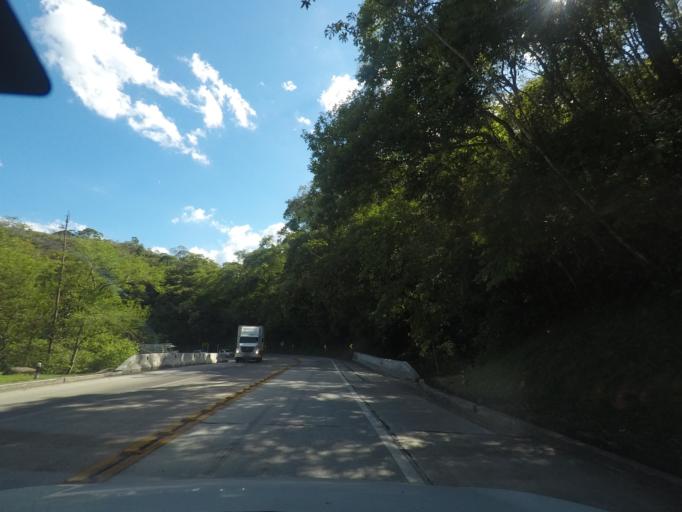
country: BR
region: Rio de Janeiro
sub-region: Guapimirim
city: Guapimirim
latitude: -22.4823
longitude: -42.9970
